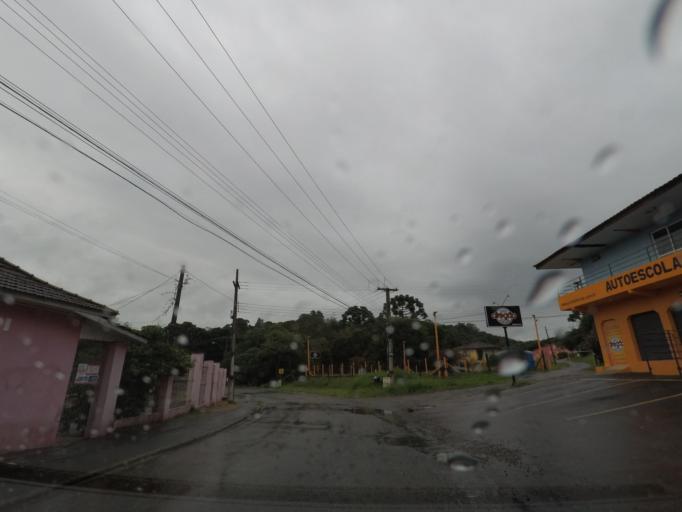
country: BR
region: Parana
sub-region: Campo Largo
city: Campo Largo
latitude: -25.4606
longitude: -49.4021
